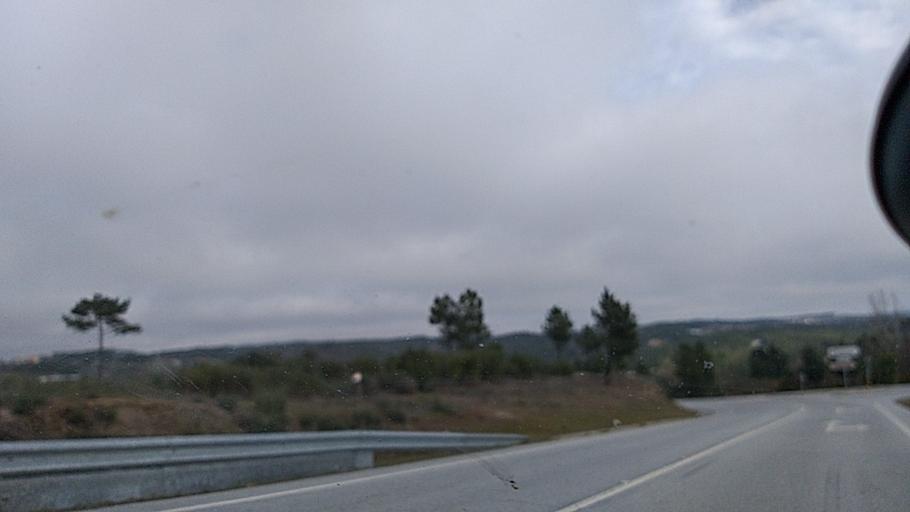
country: PT
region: Guarda
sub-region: Aguiar da Beira
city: Aguiar da Beira
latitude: 40.7730
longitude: -7.5048
